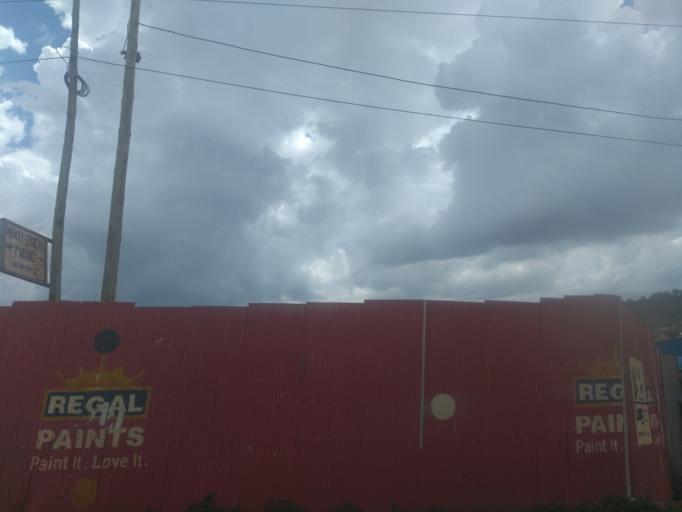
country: UG
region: Central Region
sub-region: Wakiso District
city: Kireka
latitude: 0.3414
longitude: 32.6335
